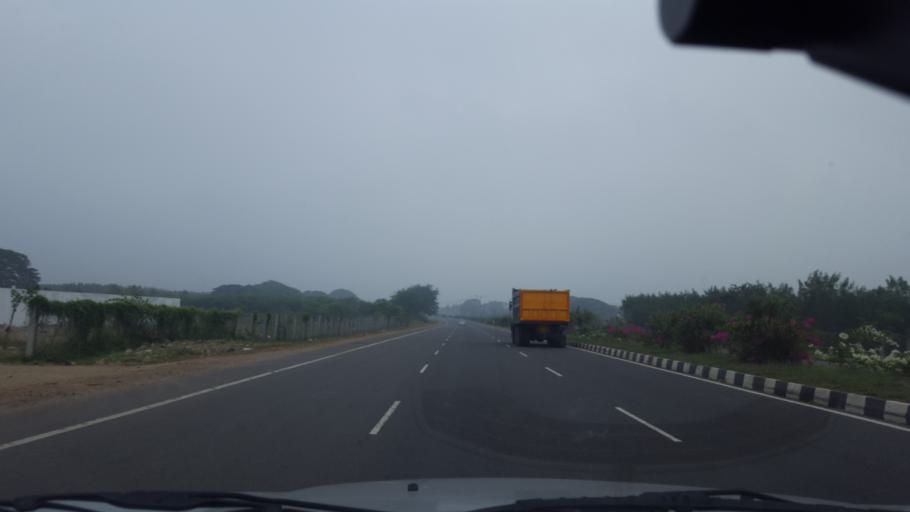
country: IN
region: Andhra Pradesh
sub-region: Prakasam
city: Addanki
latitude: 15.8150
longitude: 80.0426
